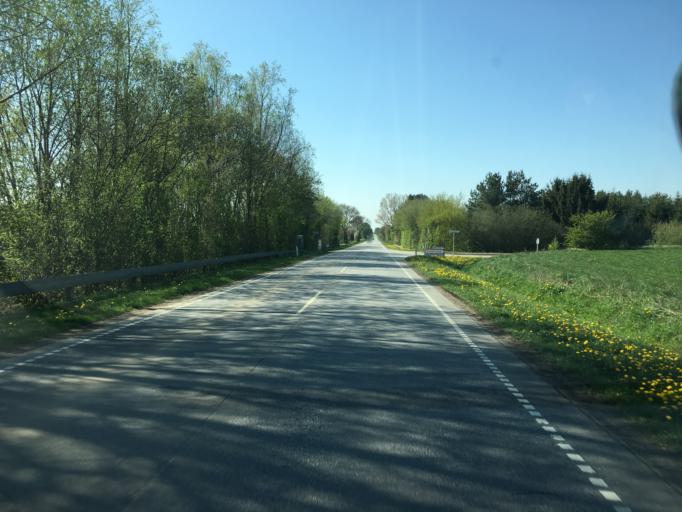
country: DK
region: South Denmark
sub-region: Haderslev Kommune
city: Vojens
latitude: 55.2974
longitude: 9.3790
